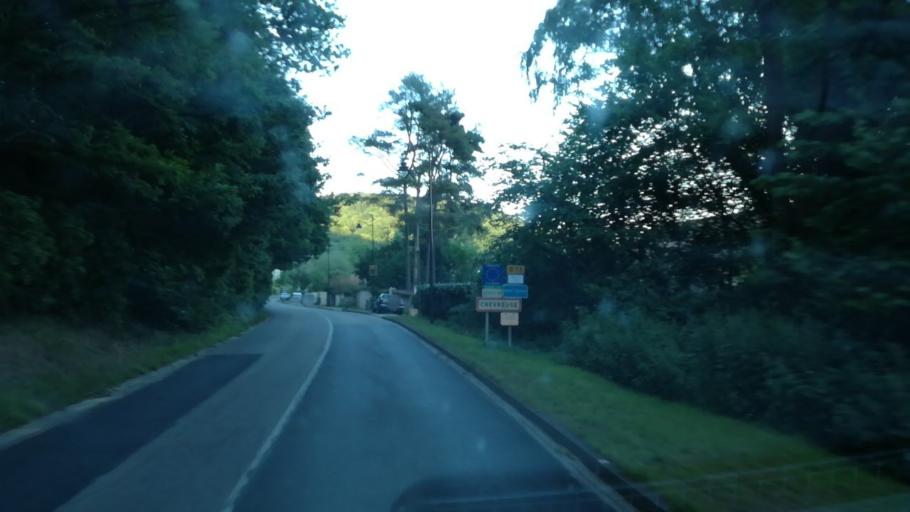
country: FR
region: Ile-de-France
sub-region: Departement des Yvelines
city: Chevreuse
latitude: 48.7125
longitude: 2.0268
